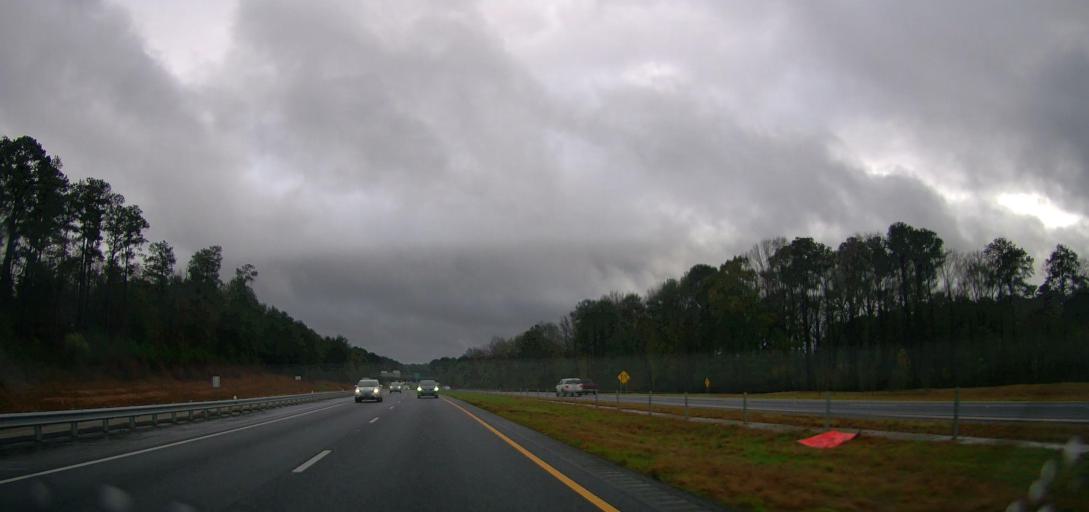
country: US
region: Georgia
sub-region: Clarke County
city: Athens
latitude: 33.9617
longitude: -83.3522
